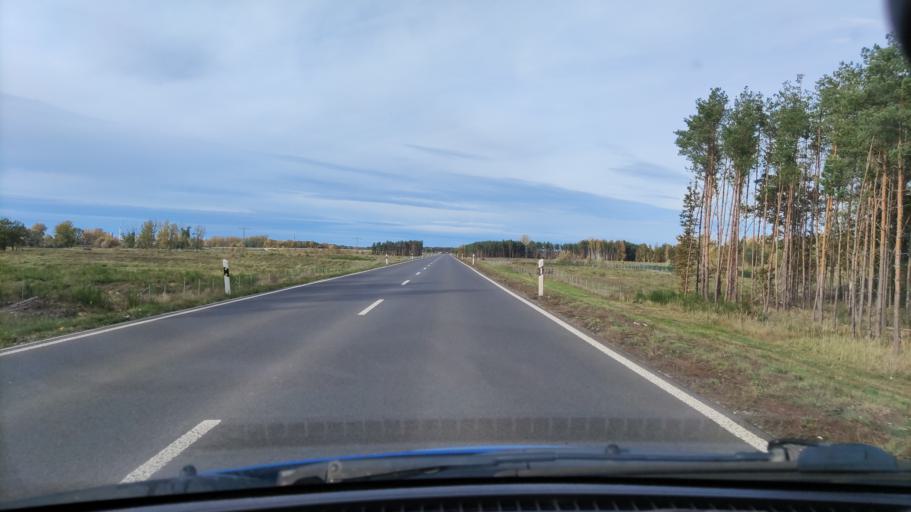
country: DE
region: Brandenburg
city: Breese
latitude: 53.0003
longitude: 11.7821
